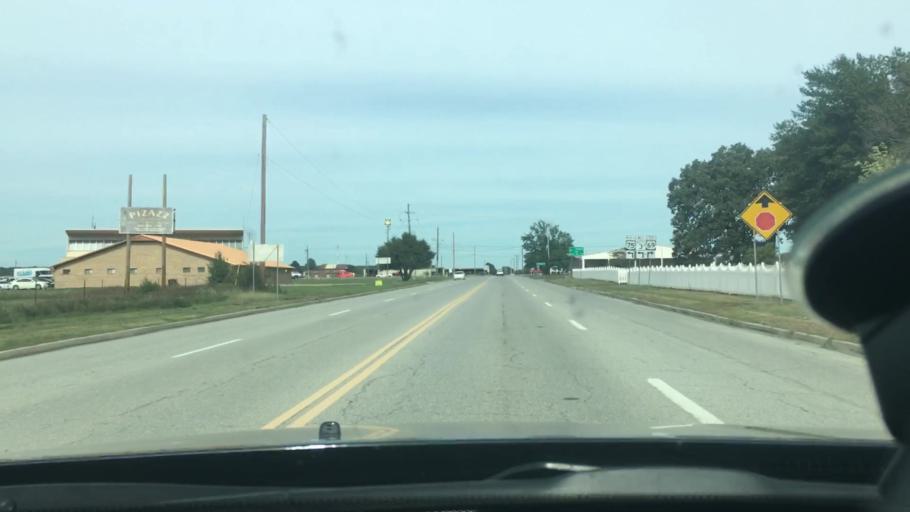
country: US
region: Oklahoma
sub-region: Atoka County
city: Atoka
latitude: 34.3916
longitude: -96.1455
